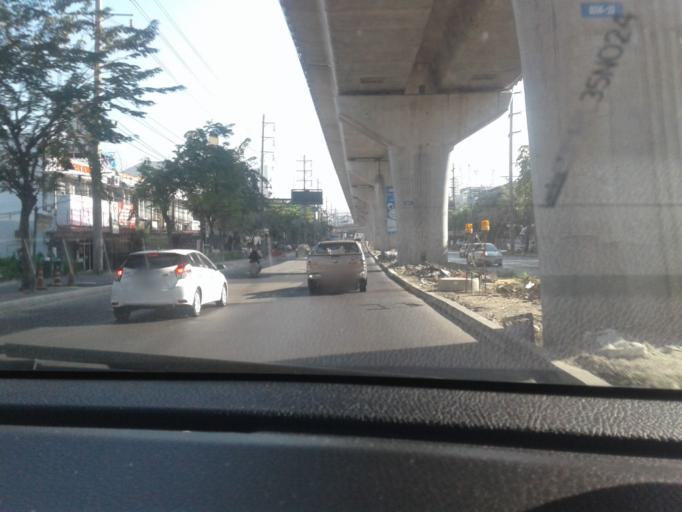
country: TH
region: Bangkok
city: Bangkok Yai
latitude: 13.7259
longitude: 100.4675
